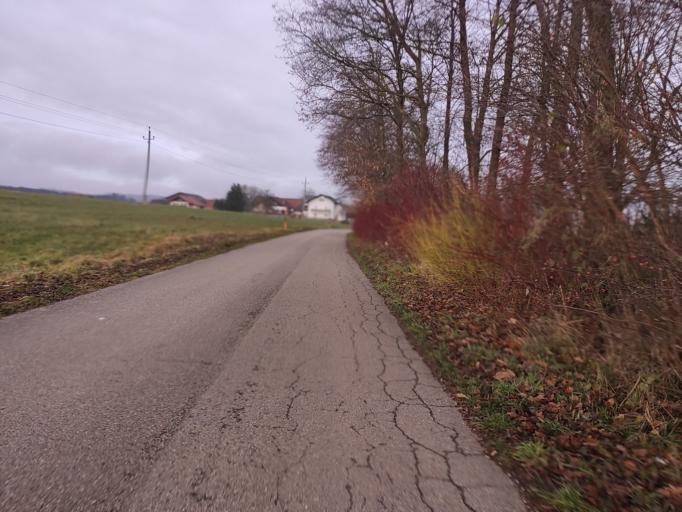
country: AT
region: Salzburg
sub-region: Politischer Bezirk Salzburg-Umgebung
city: Strasswalchen
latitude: 47.9928
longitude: 13.2352
